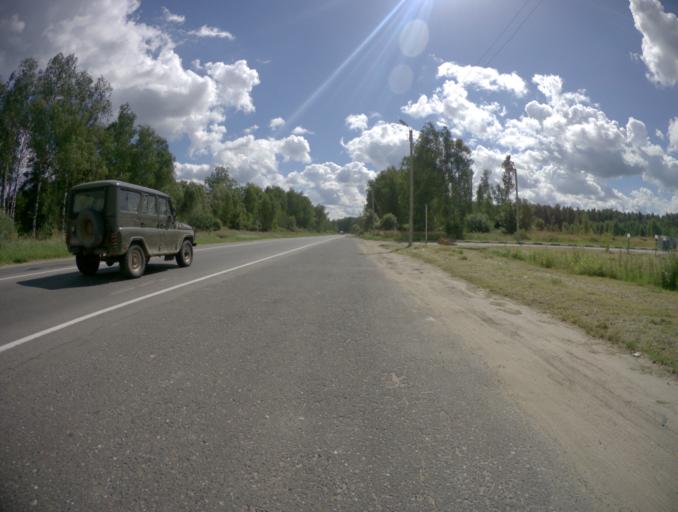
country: RU
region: Vladimir
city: Kommunar
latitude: 56.0340
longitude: 40.5580
